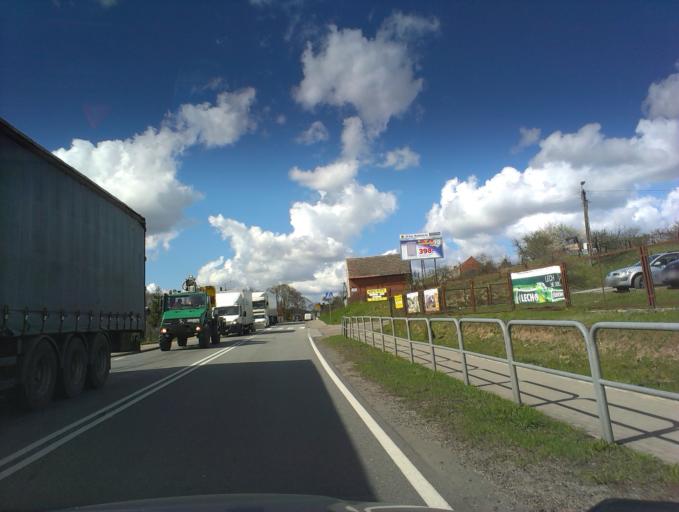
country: PL
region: West Pomeranian Voivodeship
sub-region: Powiat koszalinski
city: Bobolice
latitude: 53.8565
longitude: 16.6097
